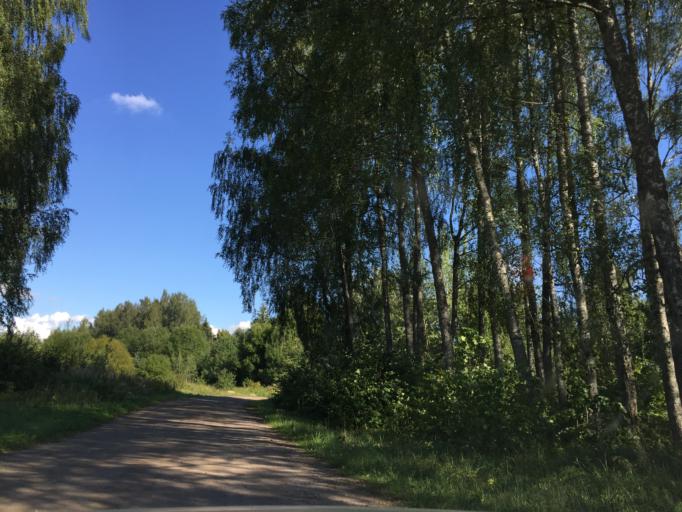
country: LV
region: Limbazu Rajons
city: Limbazi
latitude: 57.5487
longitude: 24.7659
